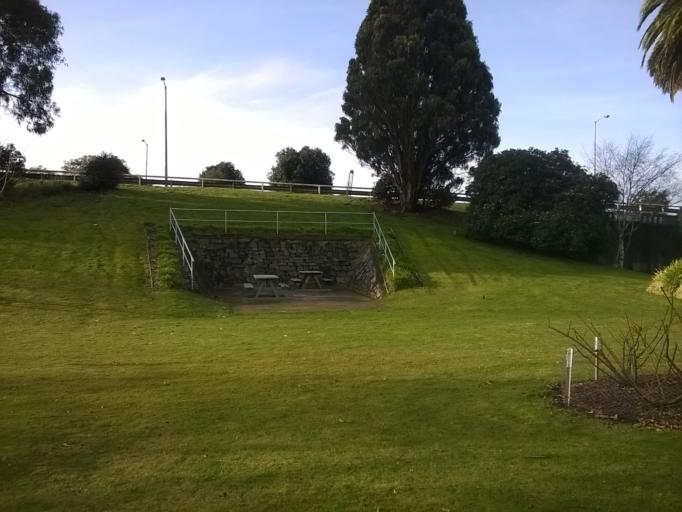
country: AU
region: Tasmania
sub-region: Burnie
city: Burnie
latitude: -41.0578
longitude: 145.9075
